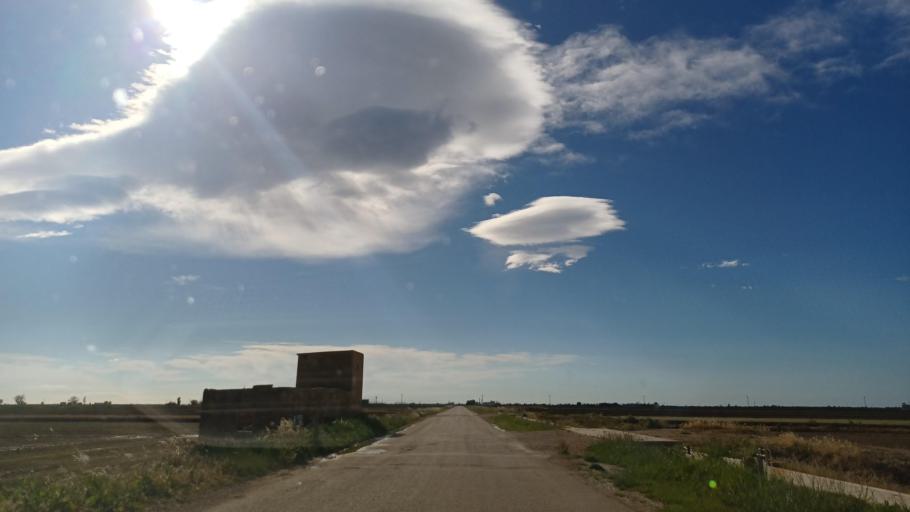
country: ES
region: Catalonia
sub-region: Provincia de Tarragona
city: Camarles
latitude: 40.7732
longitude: 0.6951
